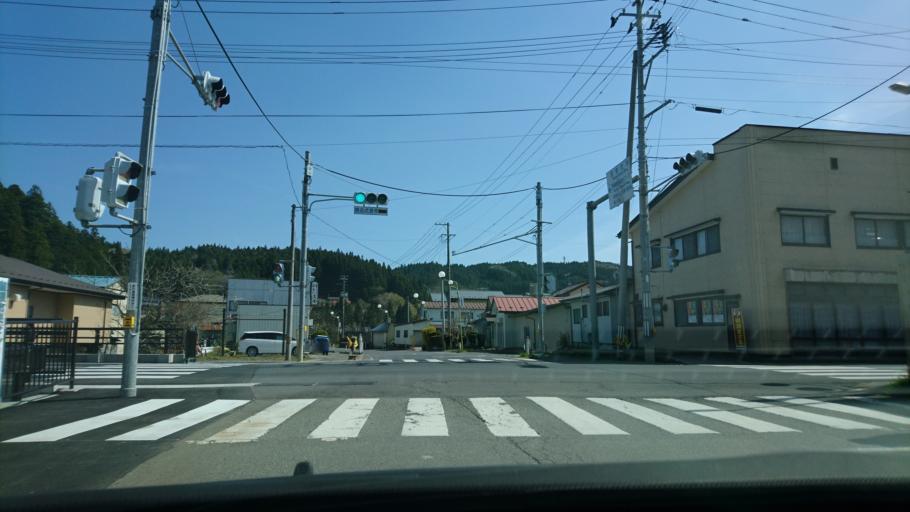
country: JP
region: Iwate
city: Ofunato
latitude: 38.9382
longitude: 141.4490
